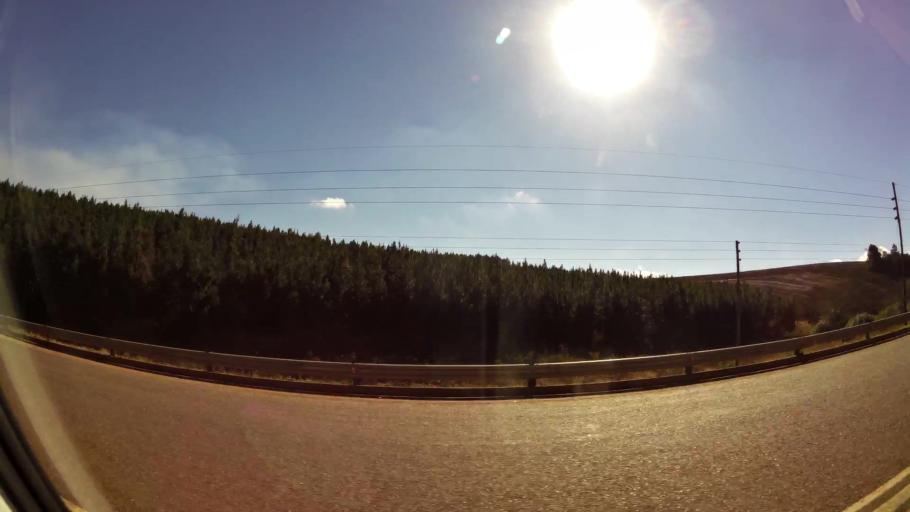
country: ZA
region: Limpopo
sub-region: Capricorn District Municipality
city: Mankoeng
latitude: -23.9373
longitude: 29.9520
